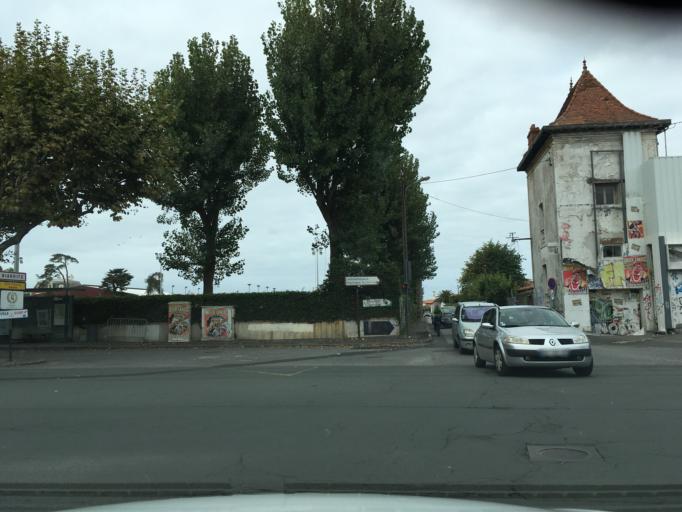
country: FR
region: Aquitaine
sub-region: Departement des Pyrenees-Atlantiques
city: Biarritz
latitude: 43.4808
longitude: -1.5348
